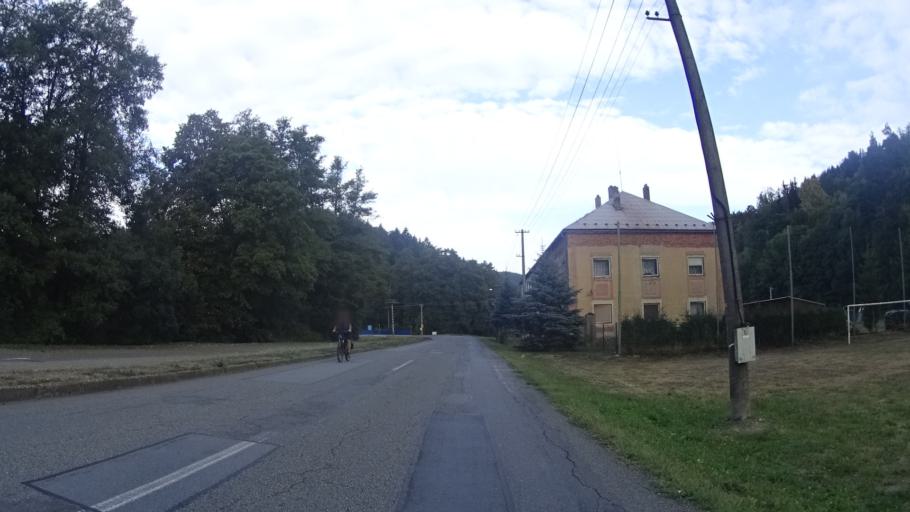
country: CZ
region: Olomoucky
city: Stity
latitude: 49.8741
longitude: 16.7711
